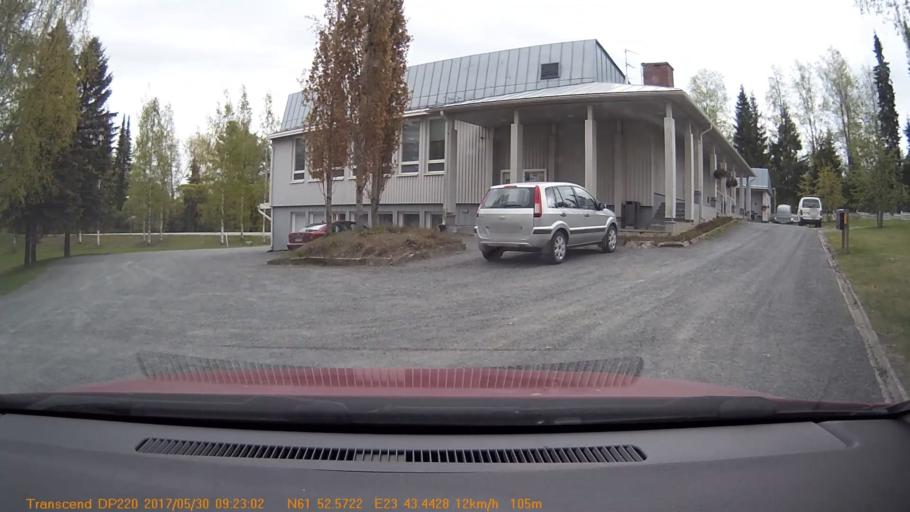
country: FI
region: Pirkanmaa
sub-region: Tampere
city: Kuru
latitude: 61.8760
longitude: 23.7246
